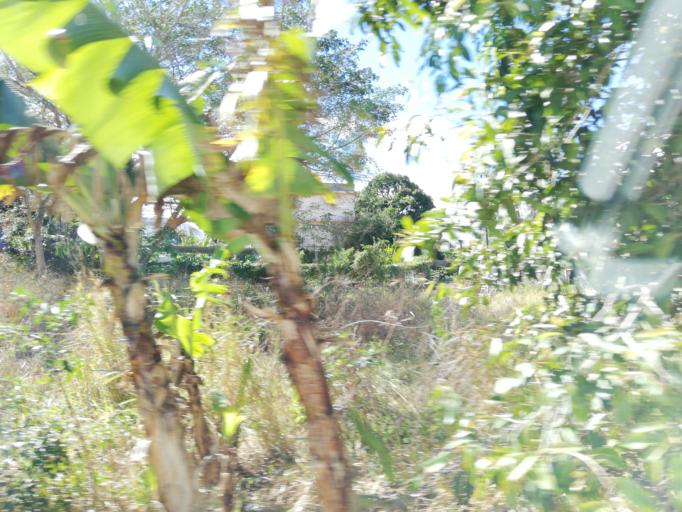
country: MU
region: Moka
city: Moka
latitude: -20.2198
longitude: 57.4669
